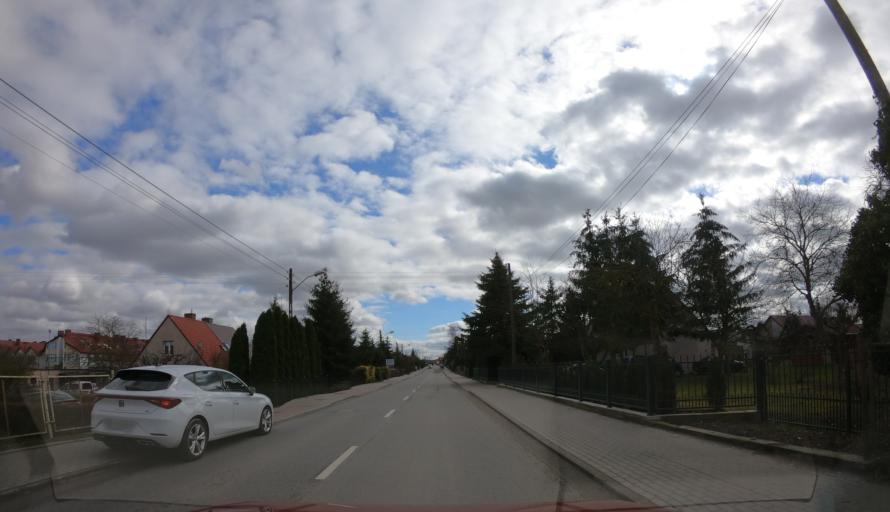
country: PL
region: West Pomeranian Voivodeship
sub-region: Powiat policki
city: Przeclaw
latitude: 53.3775
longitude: 14.4698
